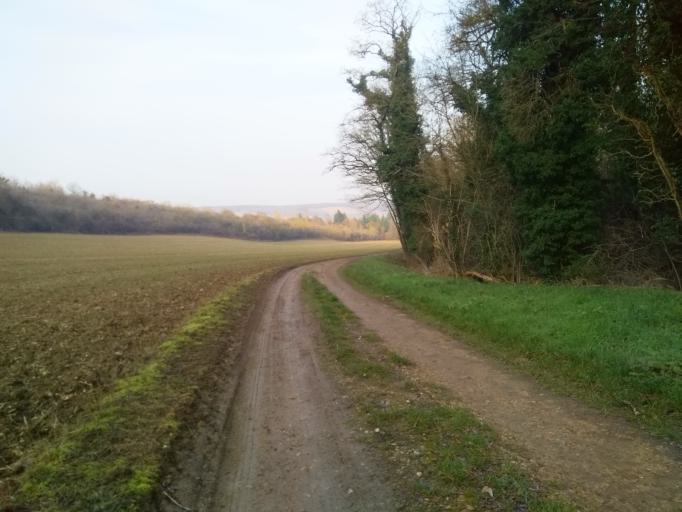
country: FR
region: Bourgogne
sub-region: Departement de l'Yonne
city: Malay-le-Grand
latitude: 48.1633
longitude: 3.3393
